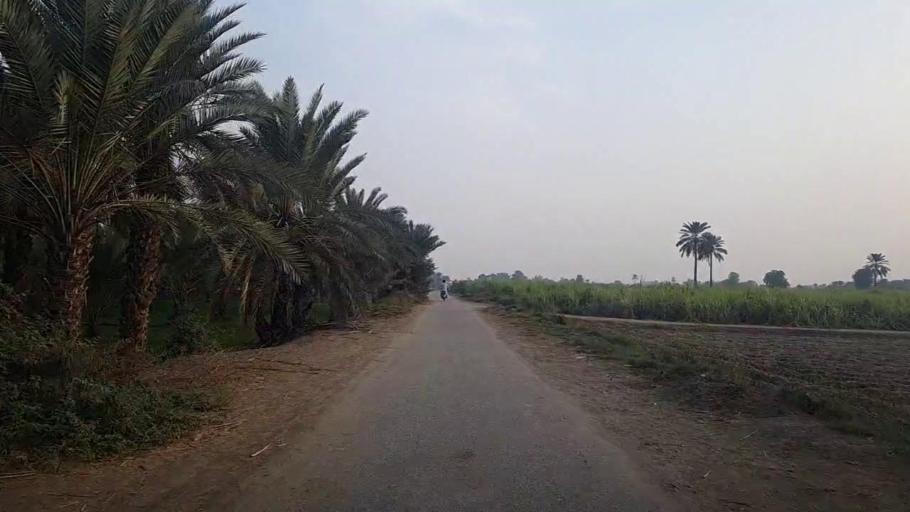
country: PK
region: Sindh
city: Kot Diji
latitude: 27.3826
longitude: 68.6625
